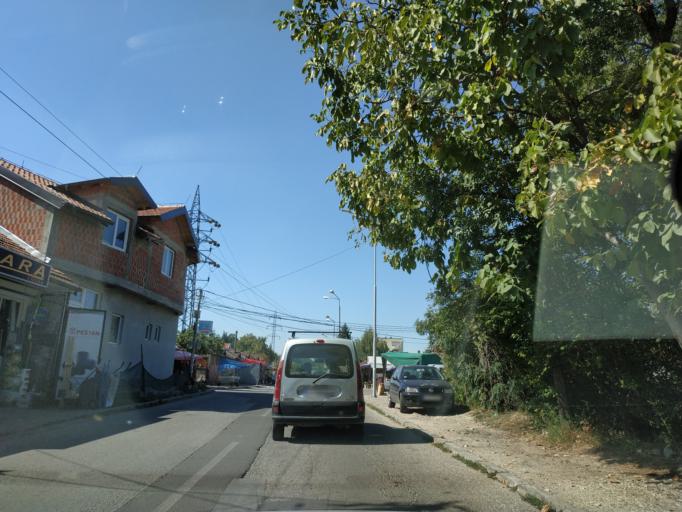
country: RS
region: Central Serbia
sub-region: Sumadijski Okrug
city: Arangelovac
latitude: 44.3010
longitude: 20.5720
